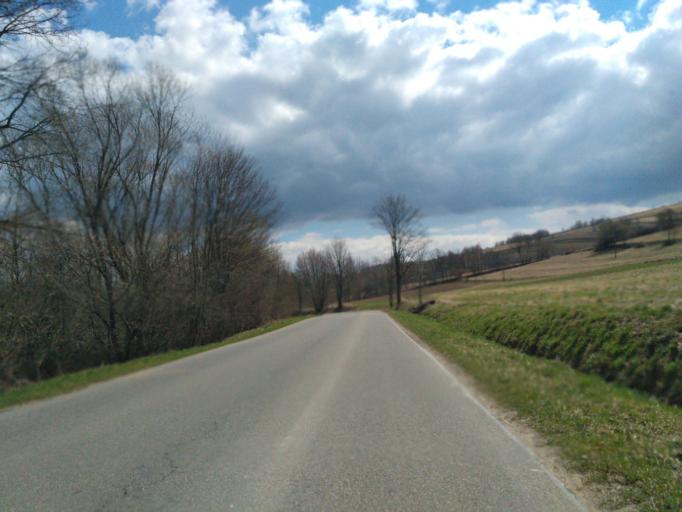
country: PL
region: Subcarpathian Voivodeship
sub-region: Powiat sanocki
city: Tyrawa Woloska
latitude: 49.5815
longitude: 22.3481
